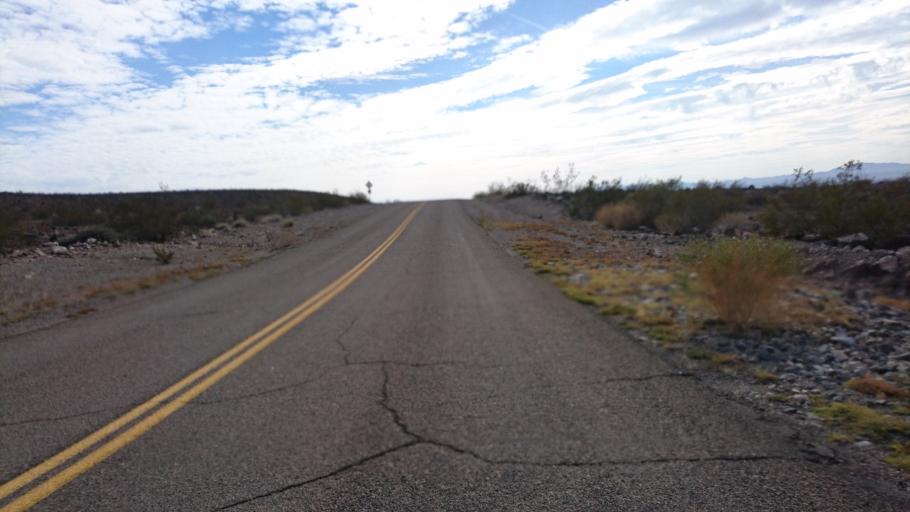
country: US
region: Arizona
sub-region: Mohave County
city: Mohave Valley
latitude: 34.9016
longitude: -114.4277
